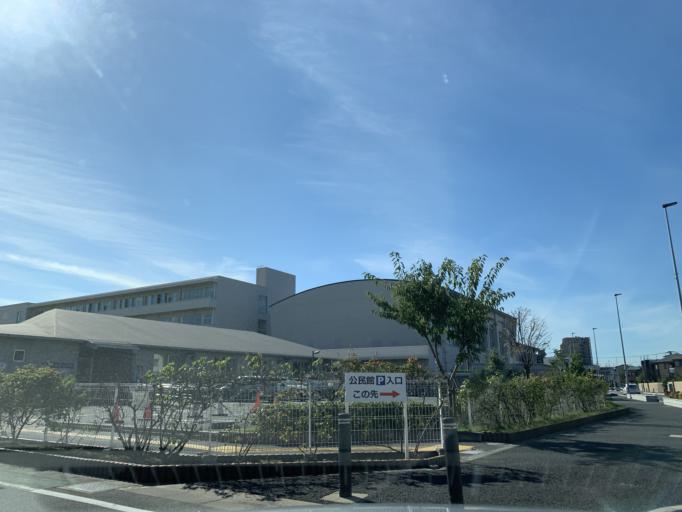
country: JP
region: Chiba
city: Matsudo
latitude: 35.7329
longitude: 139.9173
